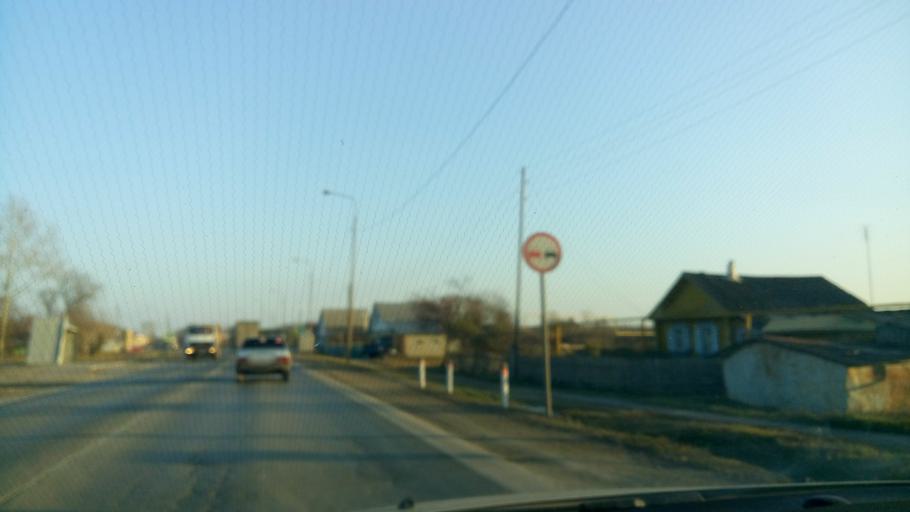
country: RU
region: Sverdlovsk
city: Bogdanovich
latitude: 56.7565
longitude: 62.0856
